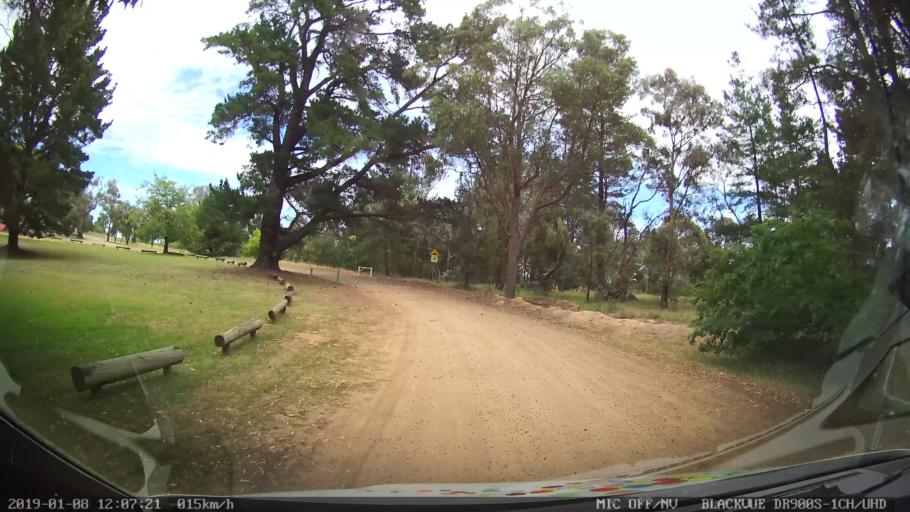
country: AU
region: New South Wales
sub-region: Armidale Dumaresq
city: Armidale
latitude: -30.4268
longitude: 151.5939
